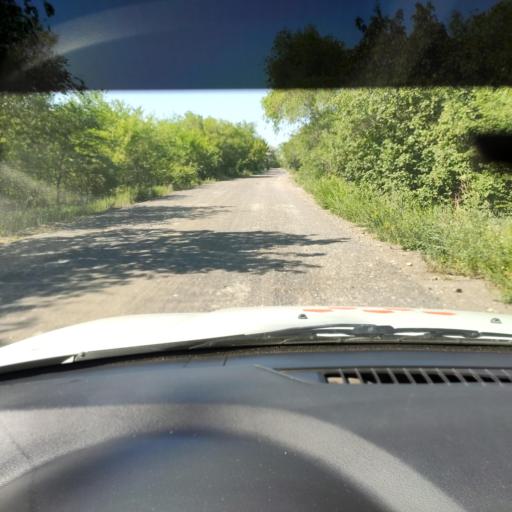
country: RU
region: Samara
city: Tol'yatti
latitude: 53.5662
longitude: 49.3679
